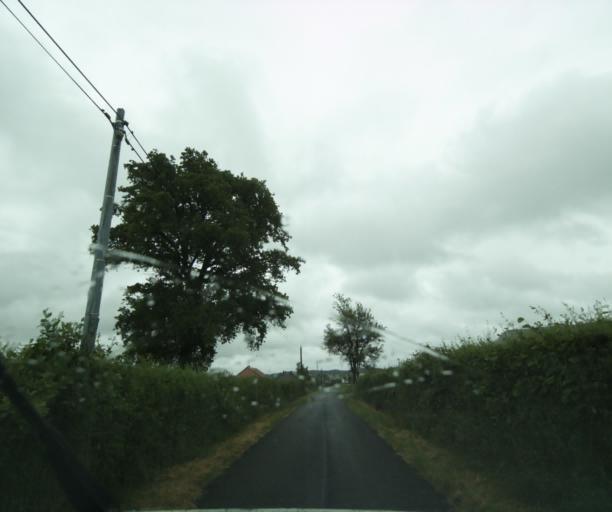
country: FR
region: Bourgogne
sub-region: Departement de Saone-et-Loire
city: Charolles
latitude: 46.4812
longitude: 4.4292
